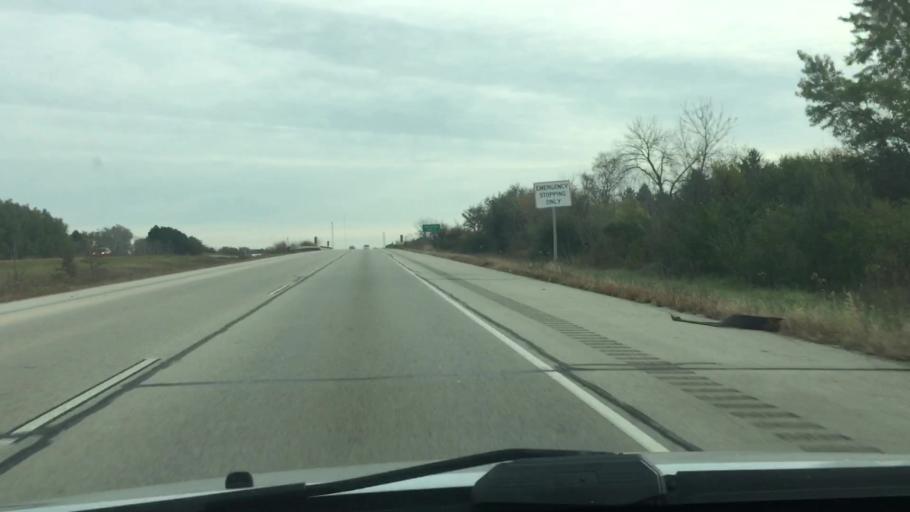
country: US
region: Wisconsin
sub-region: Waukesha County
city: Big Bend
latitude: 42.9177
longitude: -88.2009
